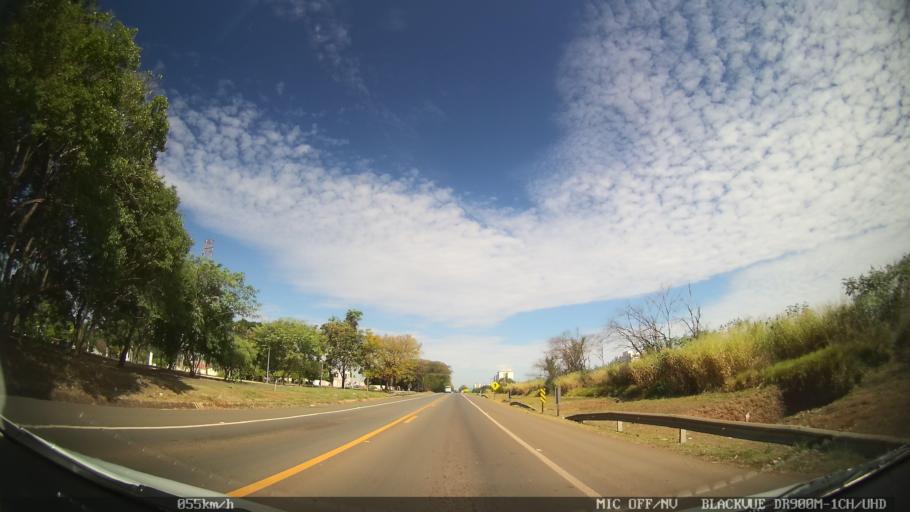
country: BR
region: Sao Paulo
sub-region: Santa Barbara D'Oeste
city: Santa Barbara d'Oeste
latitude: -22.7499
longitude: -47.4284
